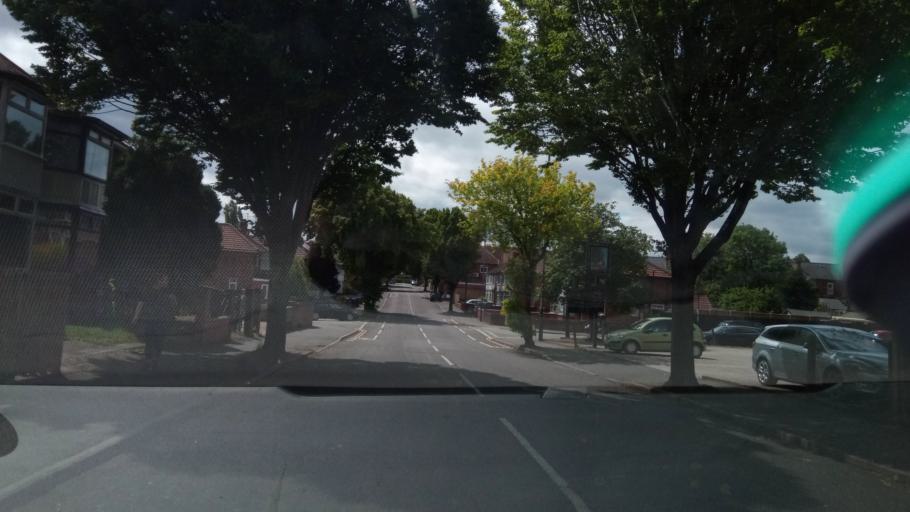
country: GB
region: England
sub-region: Derby
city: Derby
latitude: 52.9004
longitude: -1.4749
